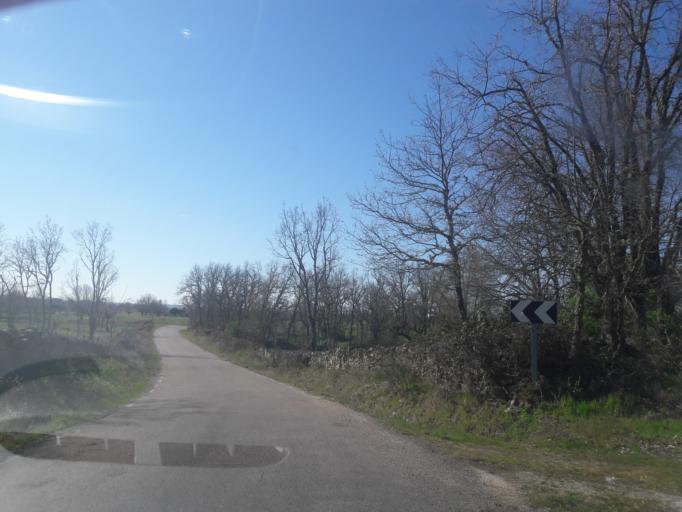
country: ES
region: Castille and Leon
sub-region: Provincia de Salamanca
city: Valsalabroso
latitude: 41.1112
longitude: -6.4838
